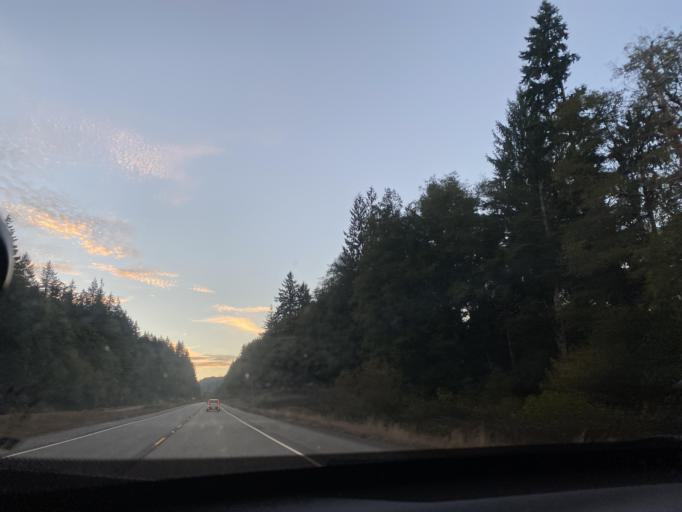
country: US
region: Washington
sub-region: Clallam County
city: Port Angeles
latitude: 48.0694
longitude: -123.6263
